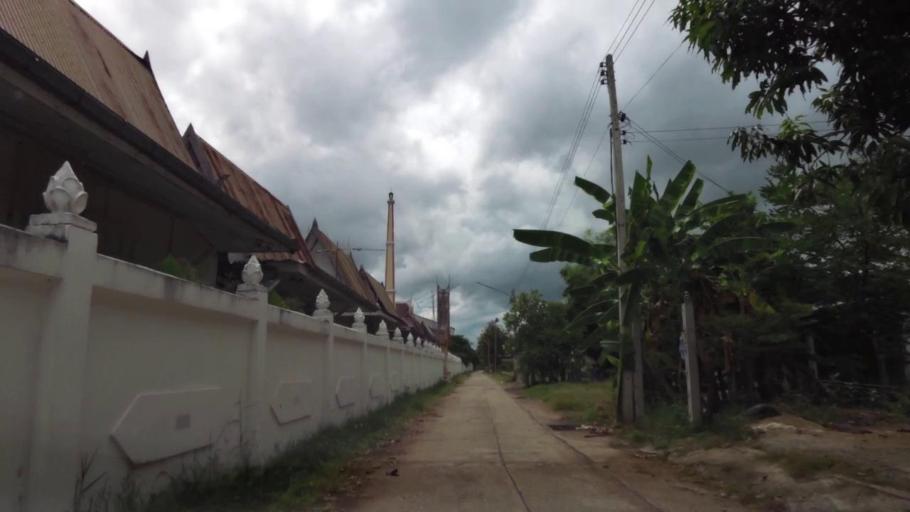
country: TH
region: Nakhon Sawan
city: Phai Sali
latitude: 15.6019
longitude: 100.6518
